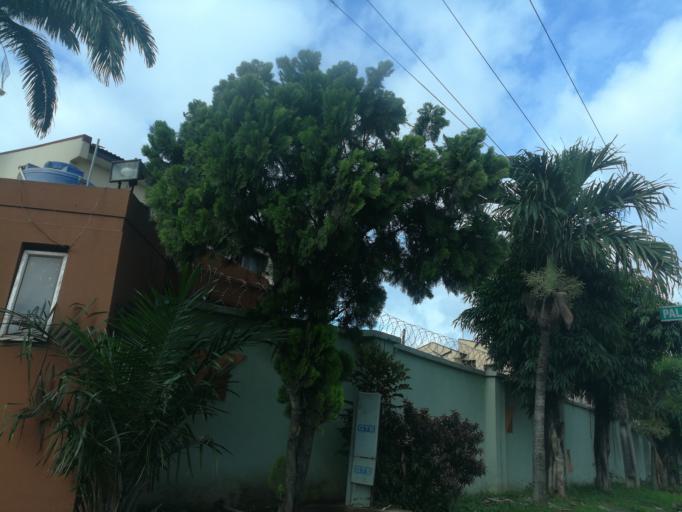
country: NG
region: Lagos
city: Ikeja
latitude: 6.6211
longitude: 3.3609
